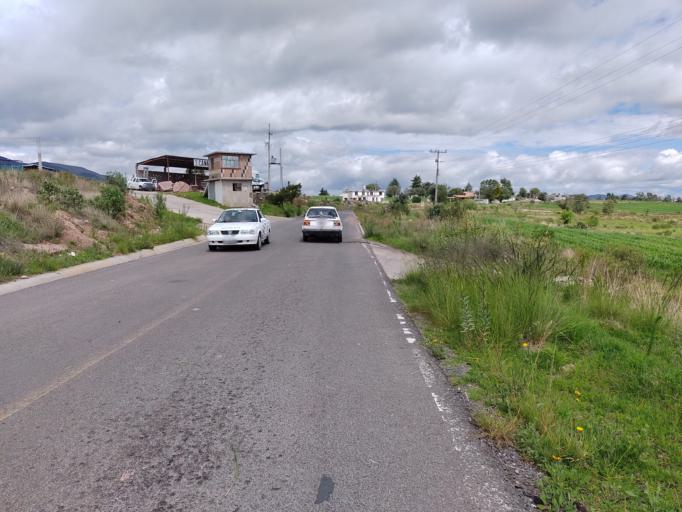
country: MX
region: Mexico
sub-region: Aculco
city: Gunyo Poniente (San Jose Gunyo)
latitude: 20.1137
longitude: -99.8703
